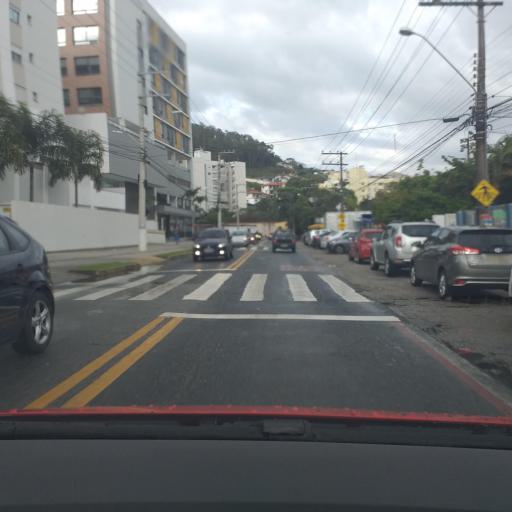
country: BR
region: Santa Catarina
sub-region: Florianopolis
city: Corrego Grande
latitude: -27.6010
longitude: -48.5033
